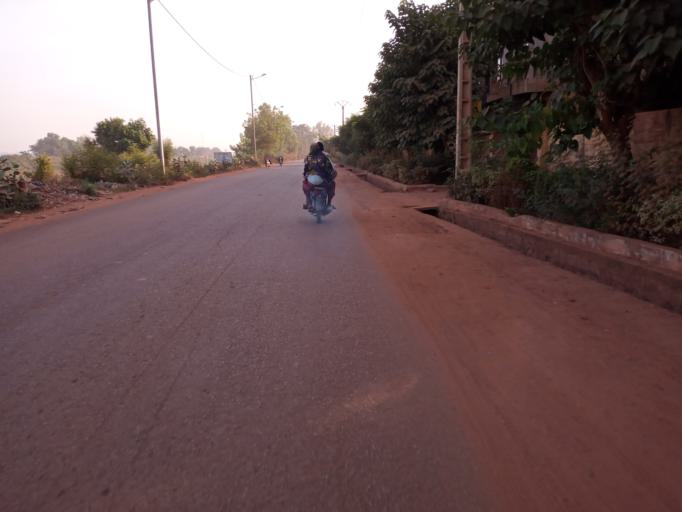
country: ML
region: Bamako
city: Bamako
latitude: 12.6331
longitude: -7.9393
